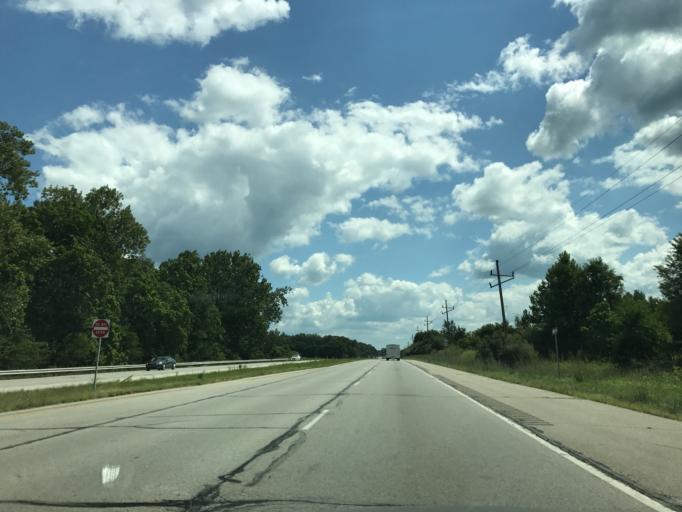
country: US
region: Indiana
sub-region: Kosciusko County
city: Pierceton
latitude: 41.2146
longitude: -85.7564
